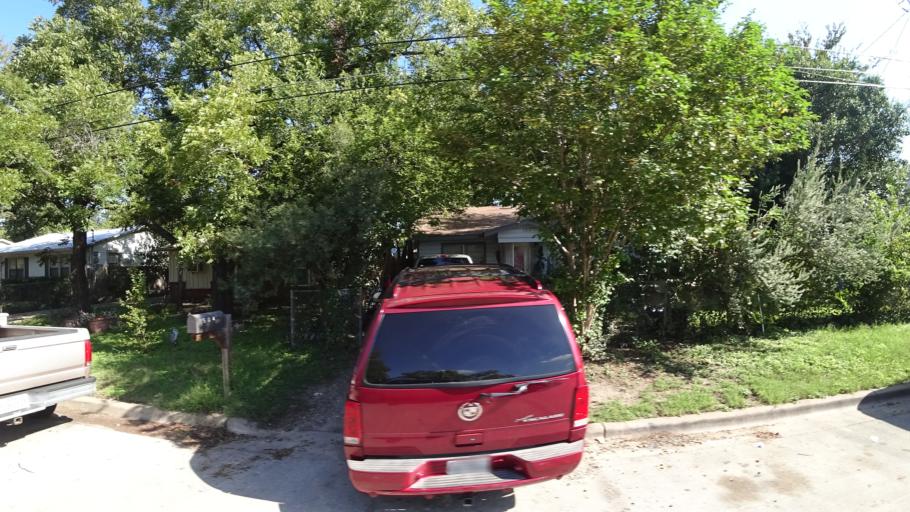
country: US
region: Texas
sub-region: Travis County
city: Austin
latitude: 30.3390
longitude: -97.7126
